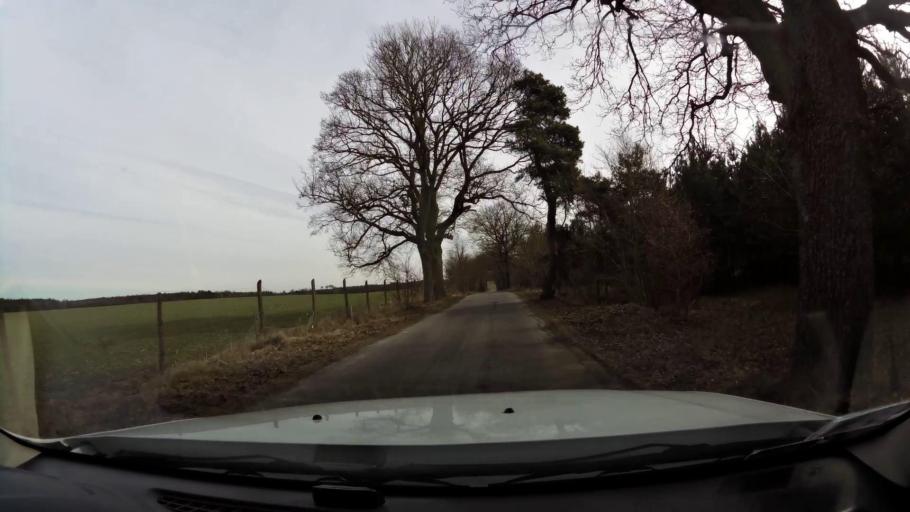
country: PL
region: West Pomeranian Voivodeship
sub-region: Powiat stargardzki
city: Insko
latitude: 53.4539
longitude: 15.6281
